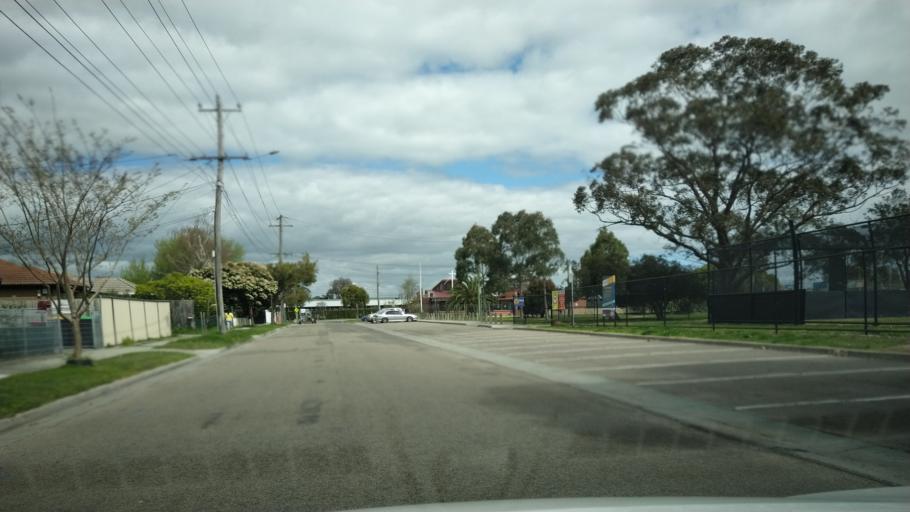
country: AU
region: Victoria
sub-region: Greater Dandenong
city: Noble Park
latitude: -37.9780
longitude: 145.1707
